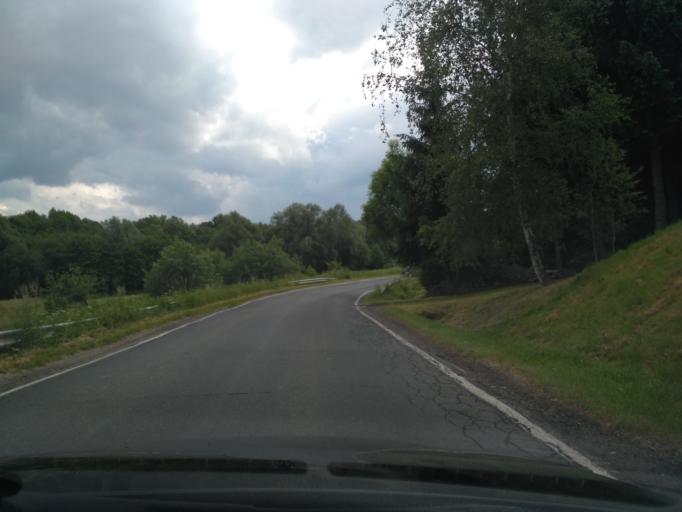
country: PL
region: Subcarpathian Voivodeship
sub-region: Powiat przeworski
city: Jawornik Polski
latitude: 49.9063
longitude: 22.3075
